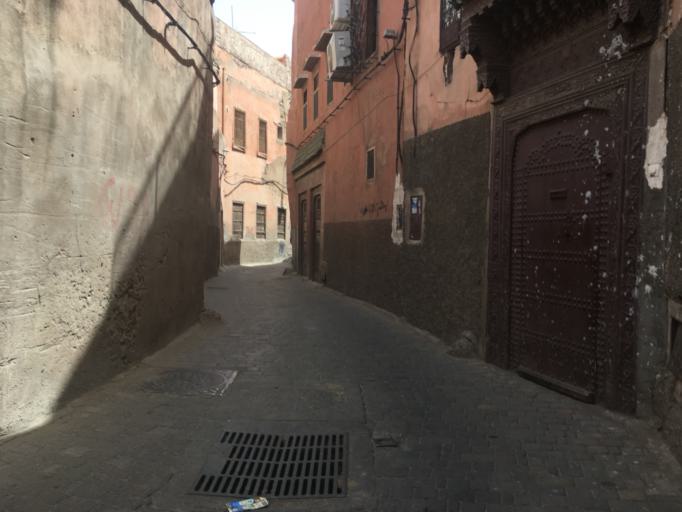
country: MA
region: Marrakech-Tensift-Al Haouz
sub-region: Marrakech
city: Marrakesh
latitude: 31.6242
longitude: -7.9843
